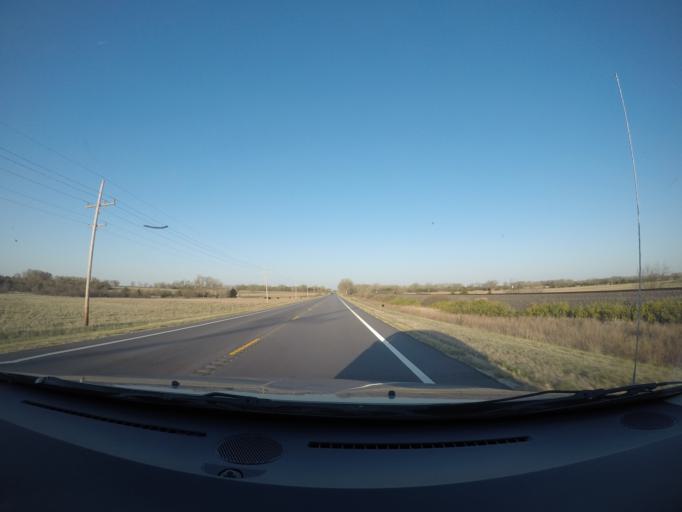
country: US
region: Kansas
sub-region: Stafford County
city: Stafford
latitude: 37.8333
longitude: -98.3744
